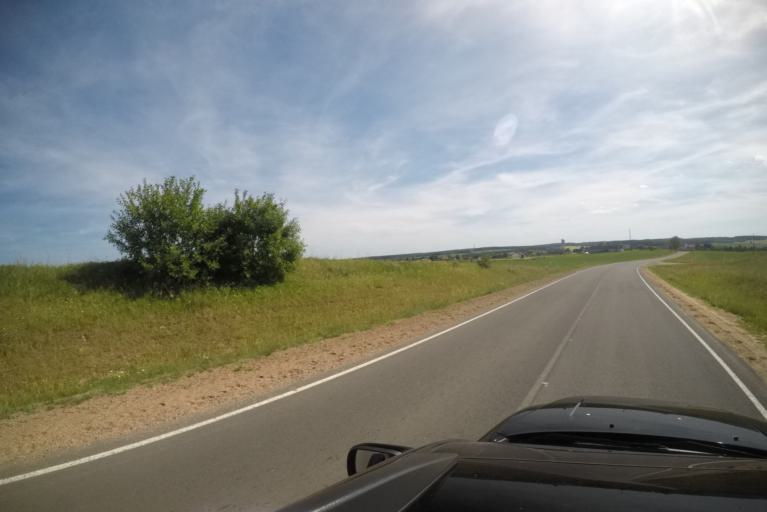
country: BY
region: Grodnenskaya
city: Hal'shany
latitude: 54.2637
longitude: 26.0245
